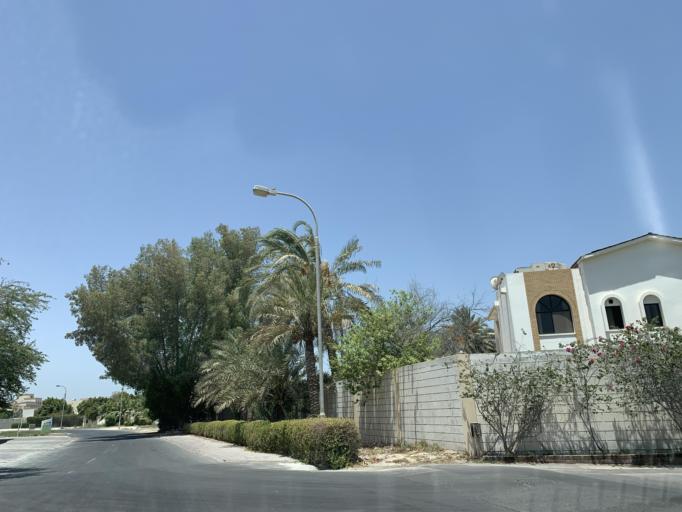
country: BH
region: Manama
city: Jidd Hafs
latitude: 26.2260
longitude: 50.4694
